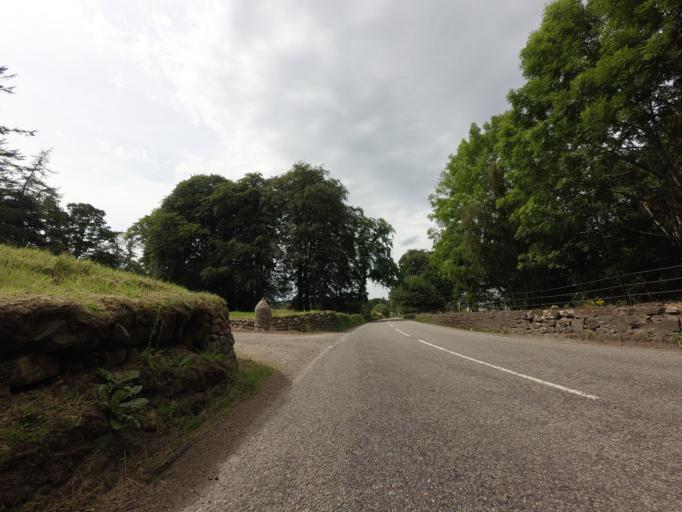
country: GB
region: Scotland
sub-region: Highland
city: Alness
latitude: 57.8550
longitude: -4.3071
